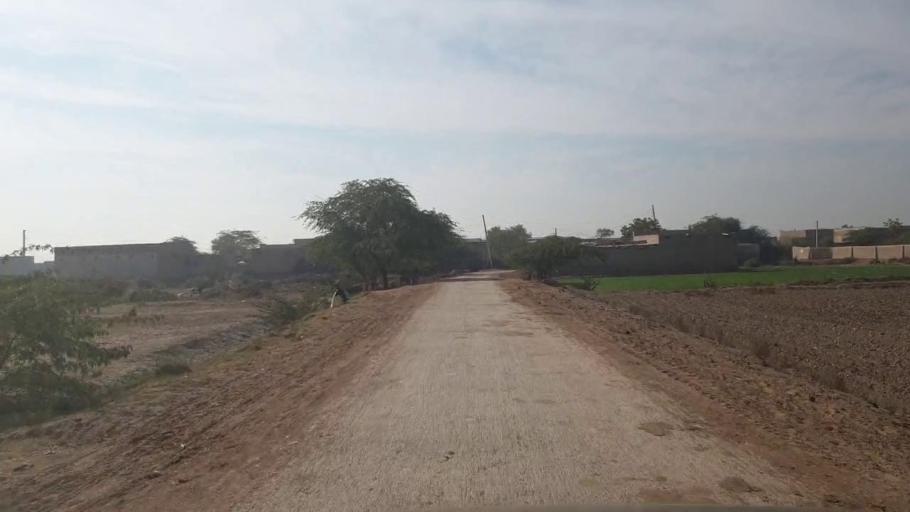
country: PK
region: Sindh
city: Shahpur Chakar
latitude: 26.1749
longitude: 68.5850
